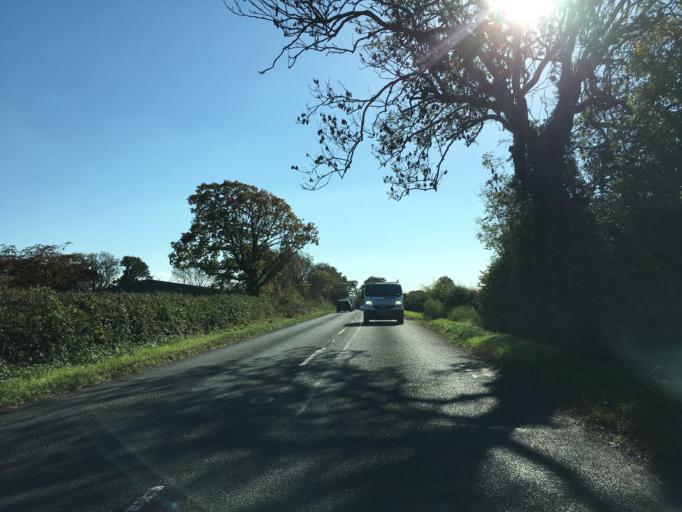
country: GB
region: England
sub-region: South Gloucestershire
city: Wickwar
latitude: 51.5777
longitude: -2.3996
